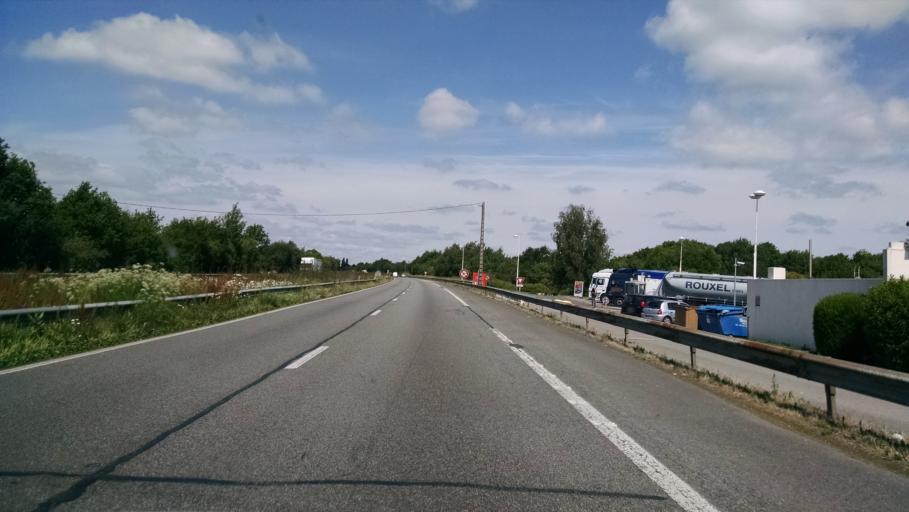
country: FR
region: Pays de la Loire
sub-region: Departement de la Loire-Atlantique
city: Le Temple-de-Bretagne
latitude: 47.3293
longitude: -1.7840
